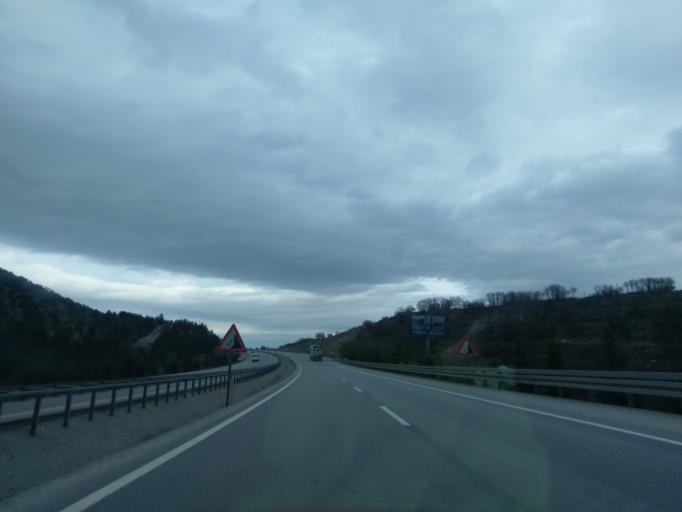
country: TR
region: Kuetahya
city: Sabuncu
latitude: 39.5924
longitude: 30.1410
